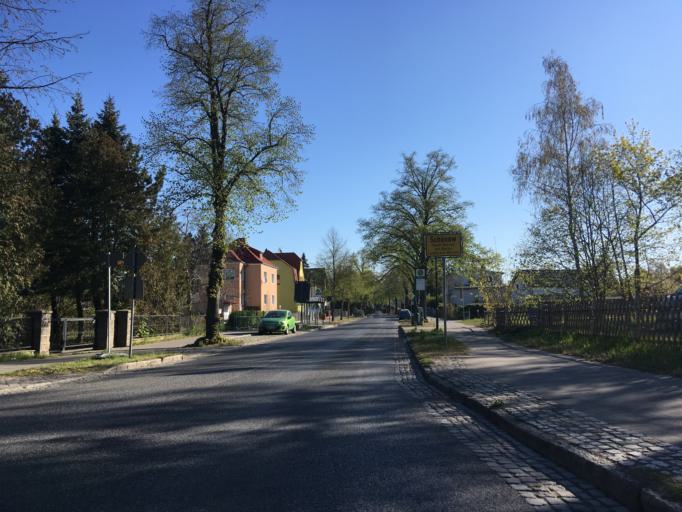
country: DE
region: Berlin
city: Buch
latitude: 52.6675
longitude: 13.5279
